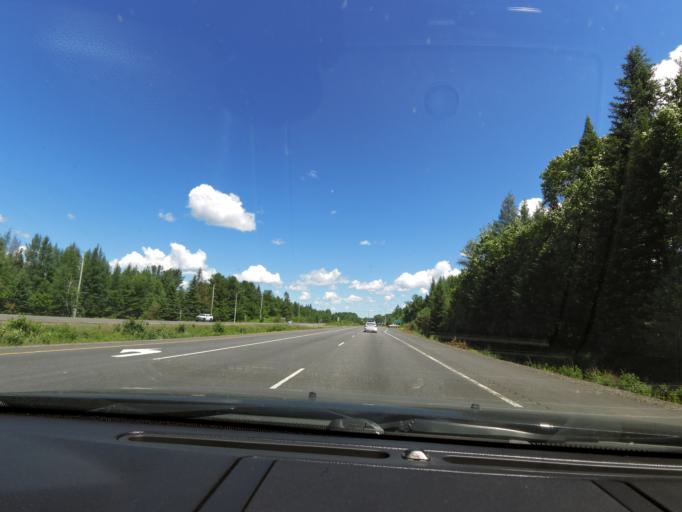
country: CA
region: Ontario
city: Bracebridge
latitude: 45.1752
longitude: -79.3117
